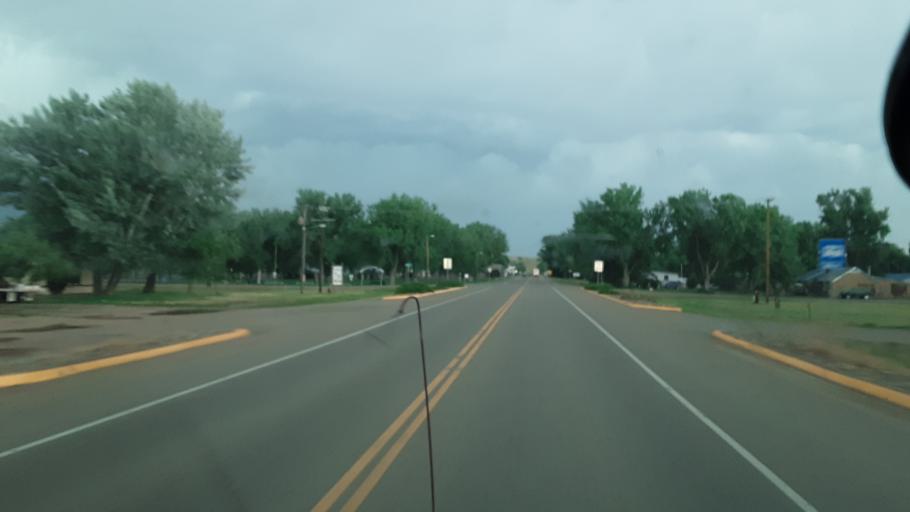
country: US
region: Montana
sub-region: Powder River County
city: Broadus
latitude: 45.4379
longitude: -105.4083
